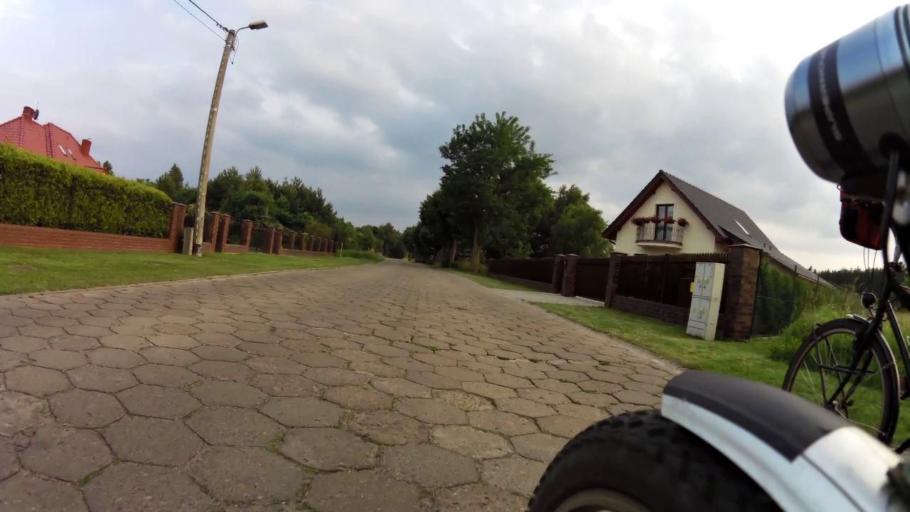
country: PL
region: West Pomeranian Voivodeship
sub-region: Powiat goleniowski
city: Stepnica
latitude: 53.6589
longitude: 14.4960
